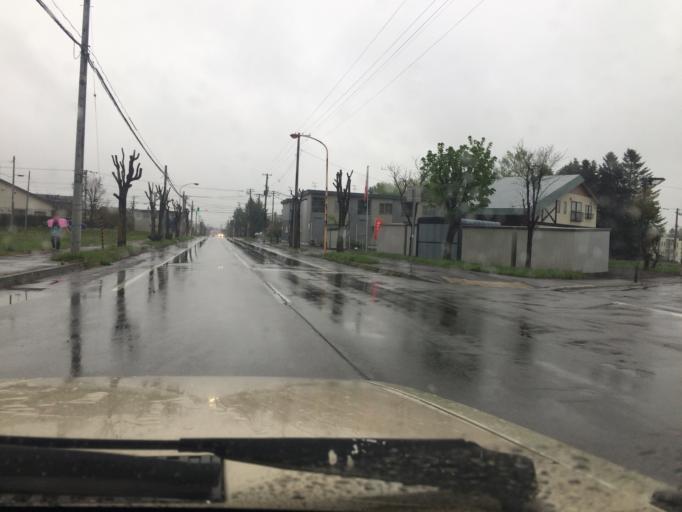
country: JP
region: Hokkaido
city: Obihiro
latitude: 42.9032
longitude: 143.0497
